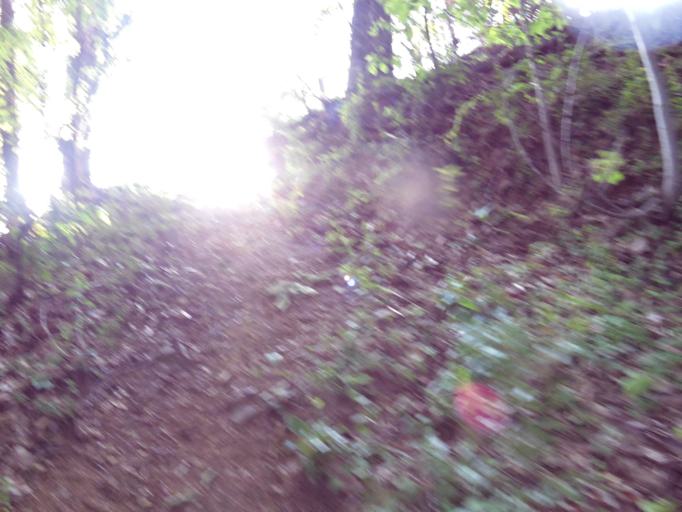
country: US
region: Tennessee
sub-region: Knox County
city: Knoxville
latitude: 36.0026
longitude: -83.9433
